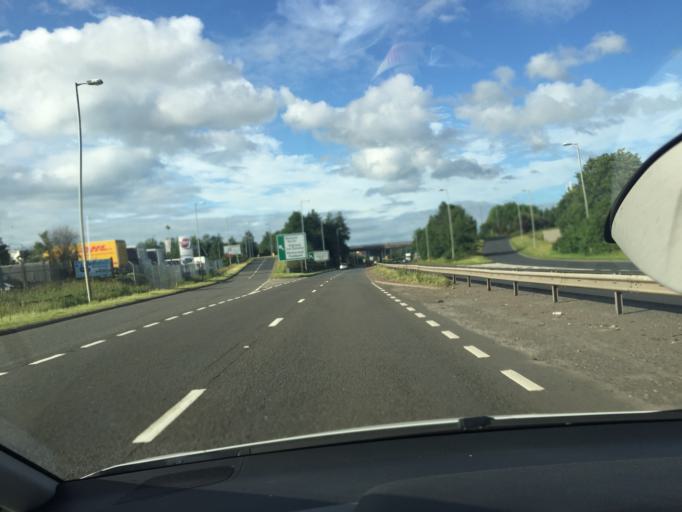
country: GB
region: Scotland
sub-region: North Lanarkshire
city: Bellshill
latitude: 55.8264
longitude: -4.0369
